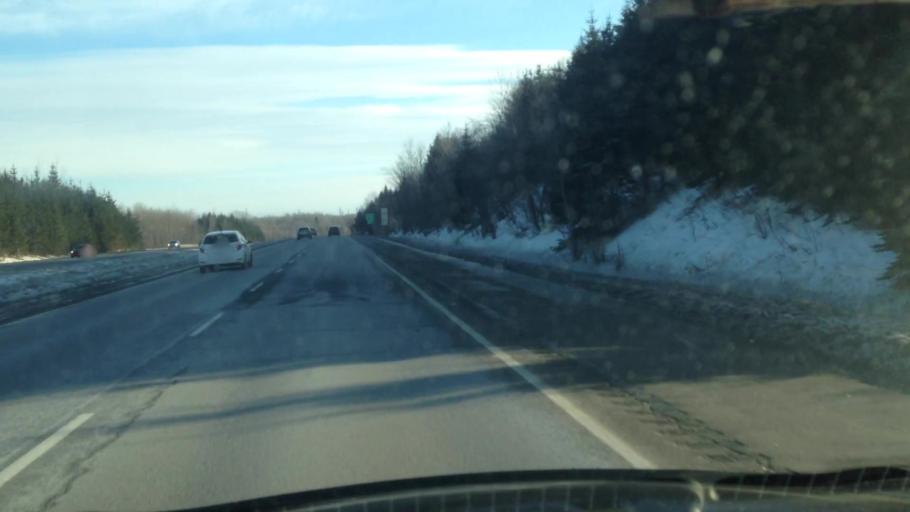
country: CA
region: Quebec
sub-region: Laurentides
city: Prevost
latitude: 45.8351
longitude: -74.0644
